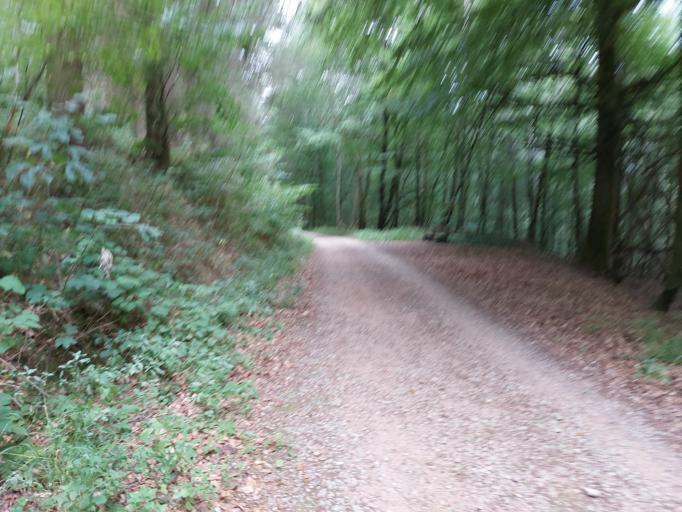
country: DE
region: Rheinland-Pfalz
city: Kordel
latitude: 49.8211
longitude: 6.6433
